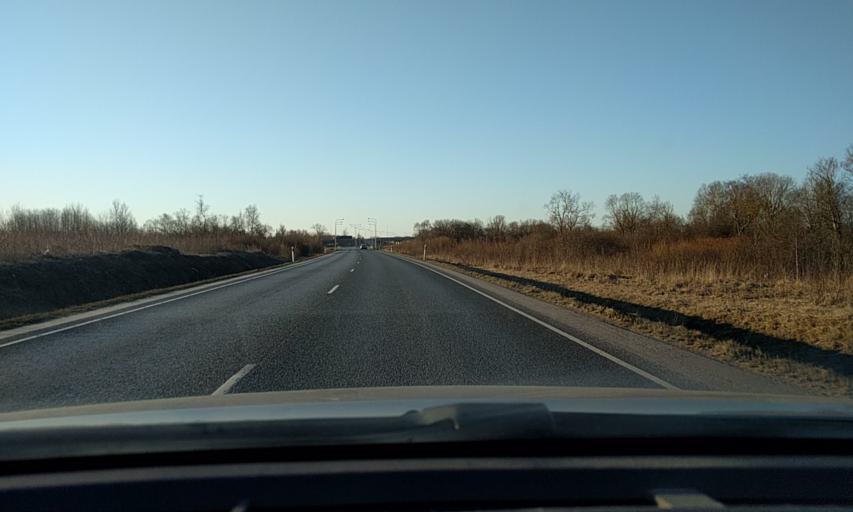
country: EE
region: Harju
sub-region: Joelaehtme vald
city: Loo
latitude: 59.4612
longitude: 24.9810
